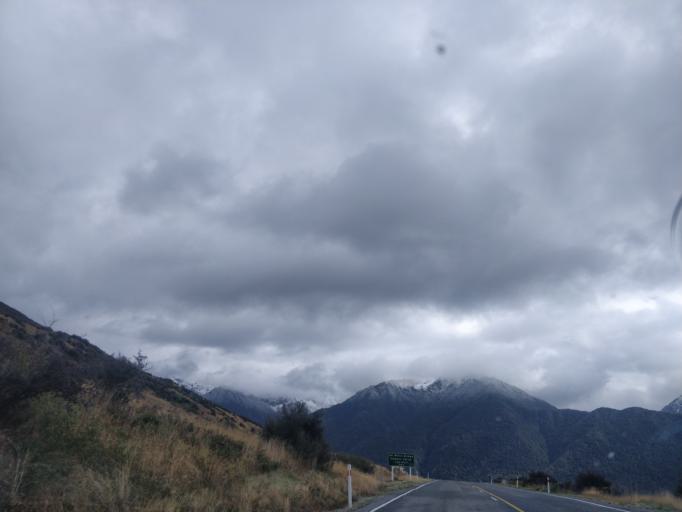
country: NZ
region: Canterbury
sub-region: Waimakariri District
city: Oxford
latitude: -43.0149
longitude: 171.7454
